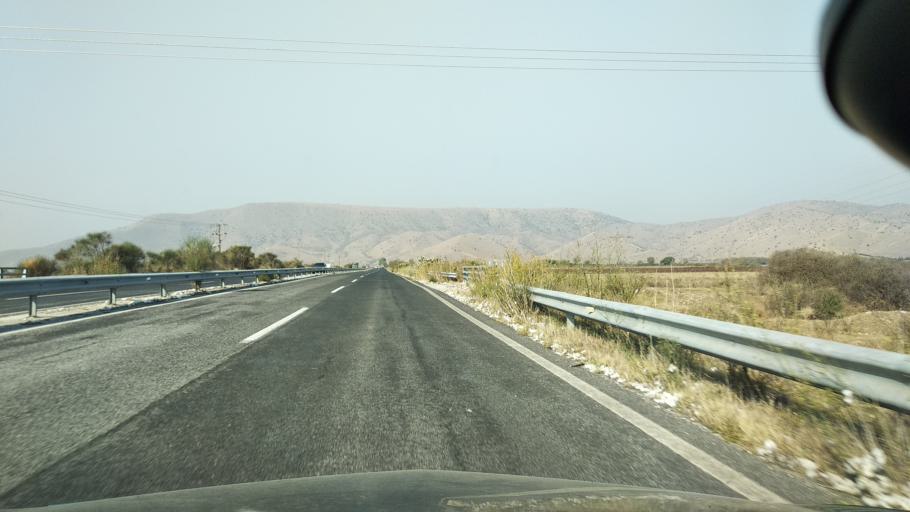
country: GR
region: Thessaly
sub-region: Trikala
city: Zarkos
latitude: 39.5954
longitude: 22.1169
